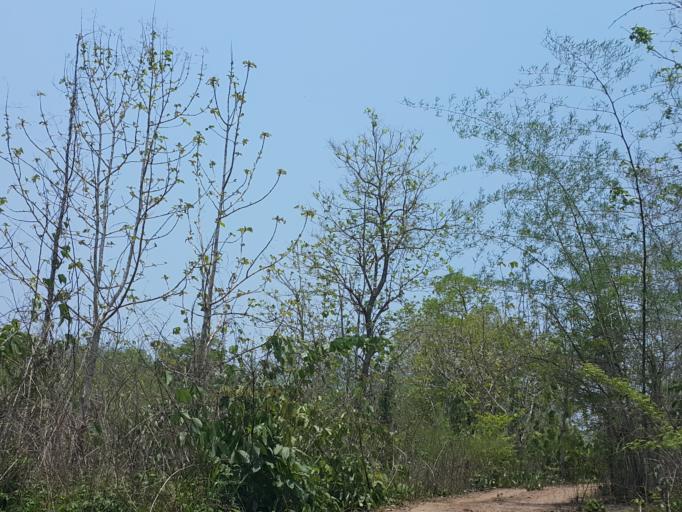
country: TH
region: Kanchanaburi
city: Sai Yok
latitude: 14.2392
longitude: 98.8712
